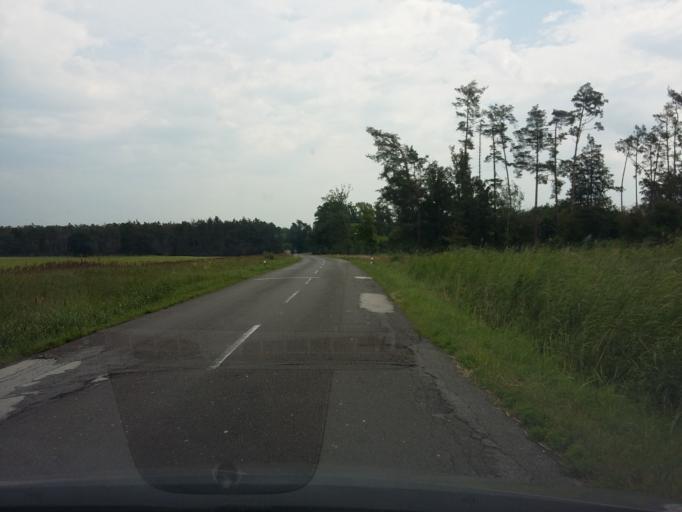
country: SK
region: Bratislavsky
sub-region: Okres Malacky
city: Malacky
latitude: 48.4566
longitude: 17.1176
